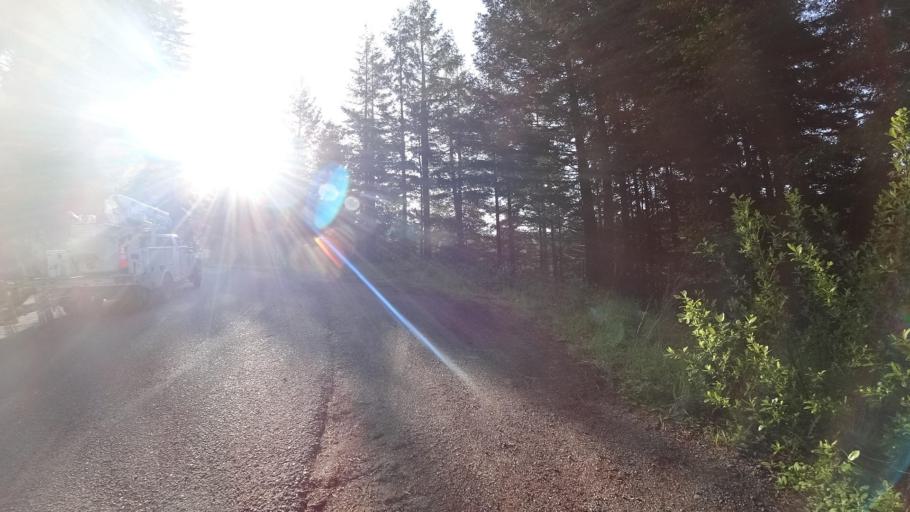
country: US
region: California
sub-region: Humboldt County
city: Bayside
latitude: 40.7549
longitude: -124.0431
